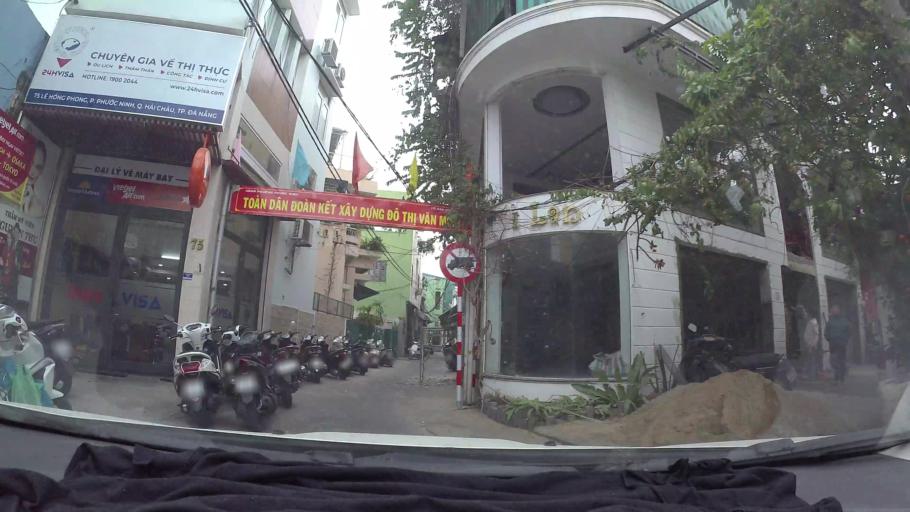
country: VN
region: Da Nang
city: Da Nang
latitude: 16.0641
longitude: 108.2194
